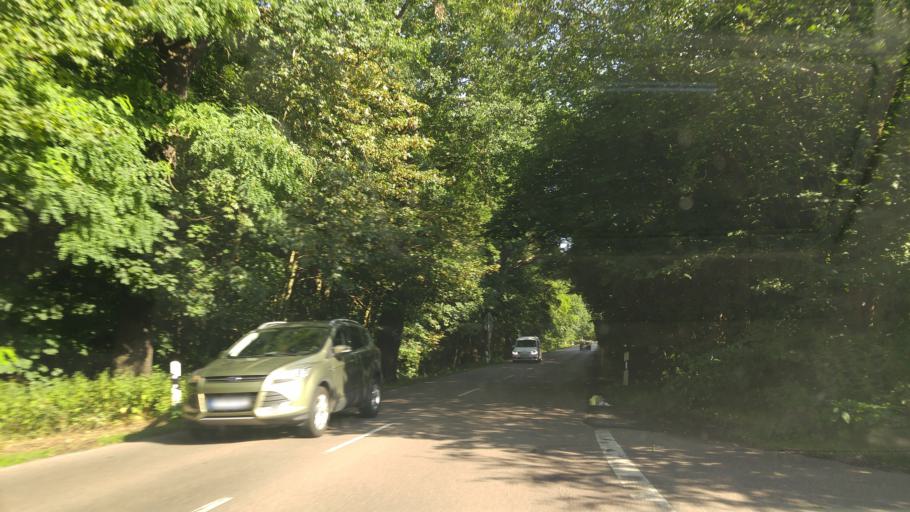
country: DE
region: Saxony-Anhalt
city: Lieskau
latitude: 51.5026
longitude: 11.8877
